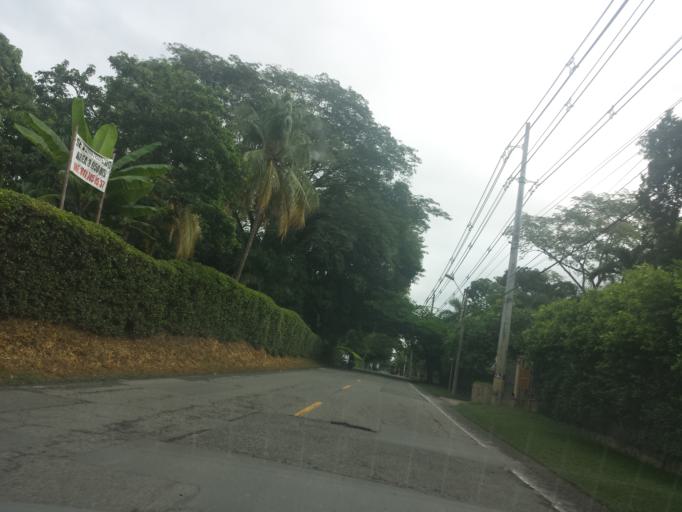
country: CO
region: Antioquia
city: Antioquia
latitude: 6.5377
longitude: -75.8192
